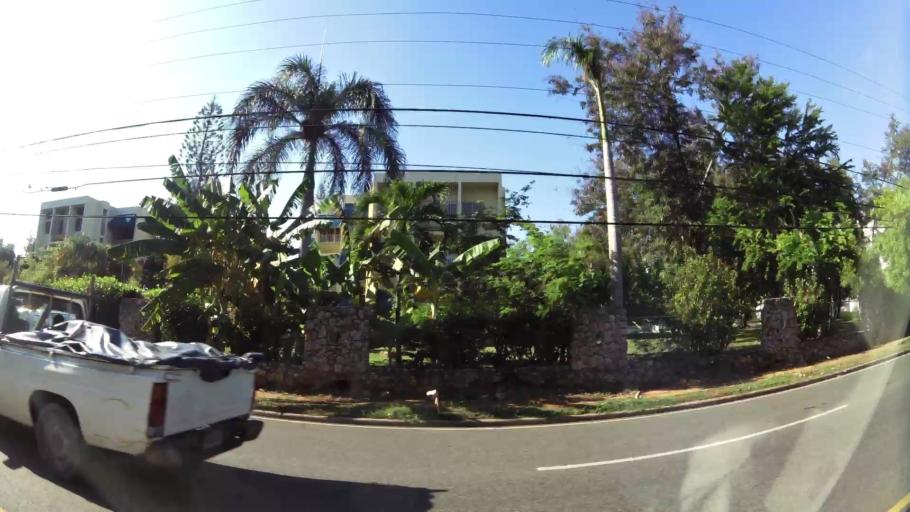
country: DO
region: Nacional
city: Bella Vista
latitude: 18.4448
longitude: -69.9516
